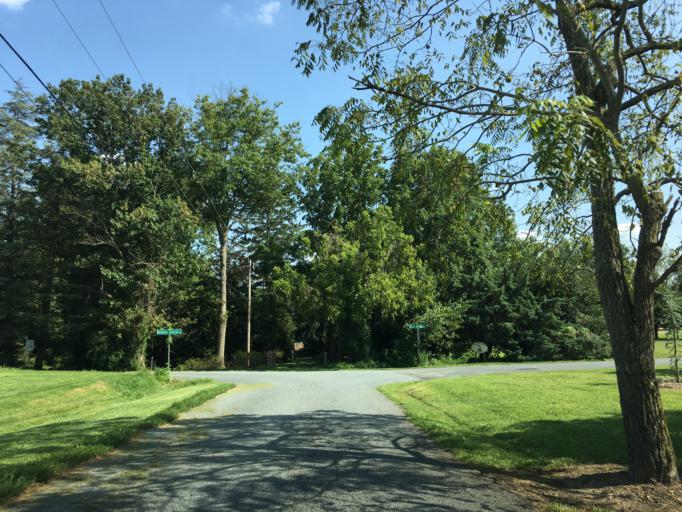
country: US
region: Maryland
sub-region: Cecil County
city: North East
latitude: 39.5190
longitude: -75.8991
